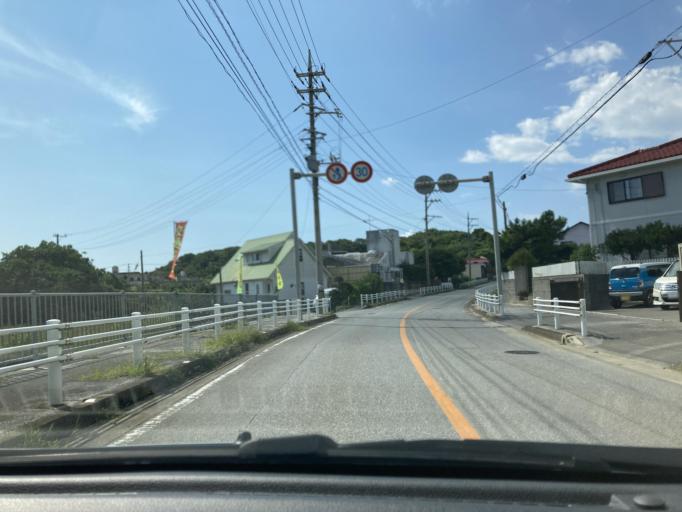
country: JP
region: Okinawa
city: Tomigusuku
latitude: 26.1510
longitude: 127.7917
